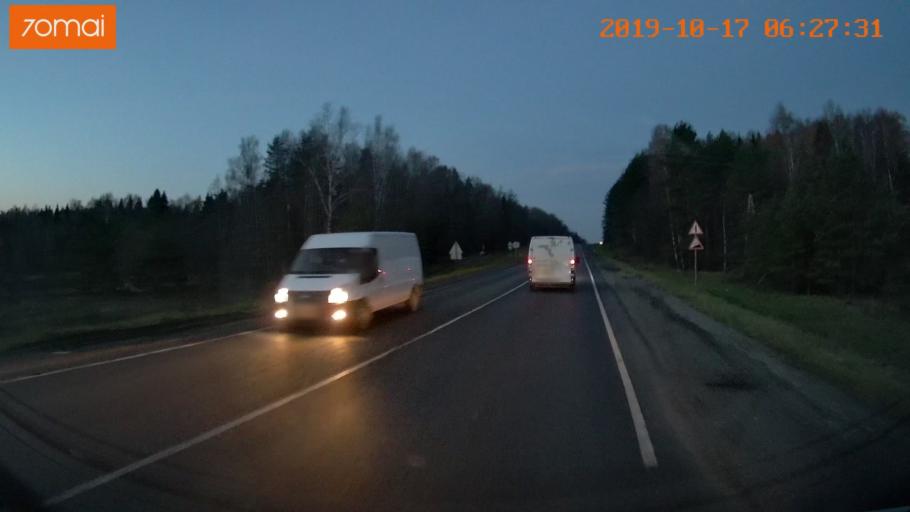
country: RU
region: Ivanovo
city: Lezhnevo
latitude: 56.7593
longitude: 40.7798
